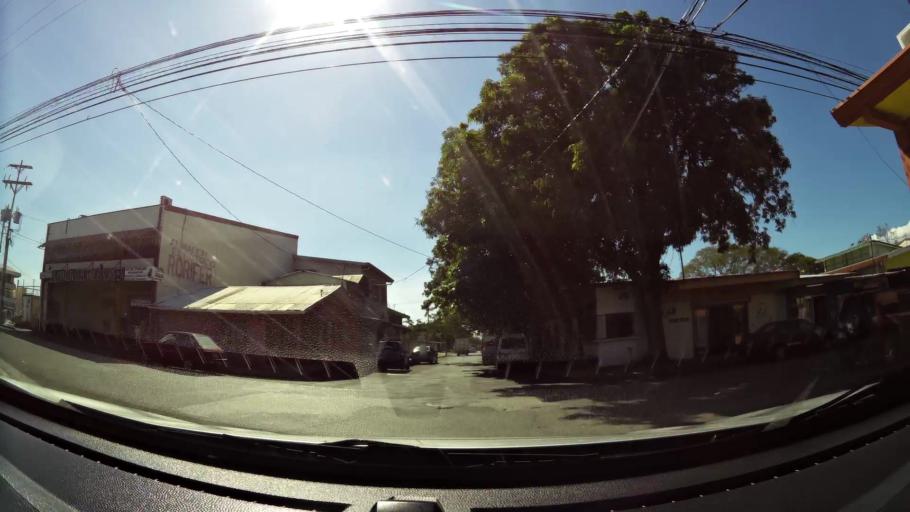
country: CR
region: Guanacaste
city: Liberia
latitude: 10.6319
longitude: -85.4425
